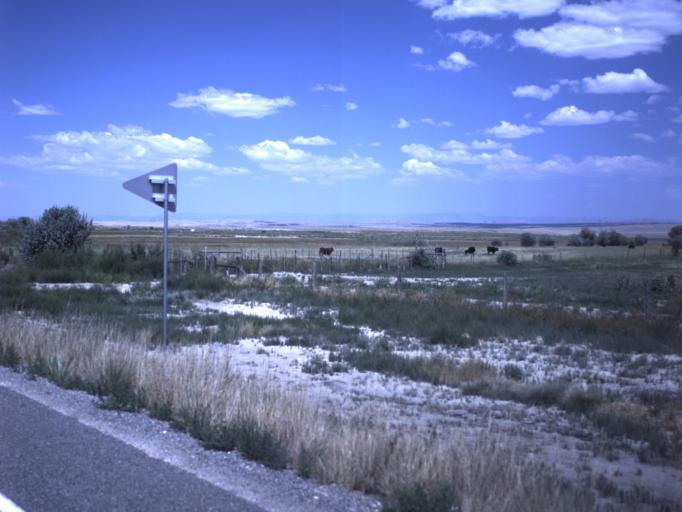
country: US
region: Utah
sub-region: Emery County
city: Castle Dale
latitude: 39.2242
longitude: -110.9963
